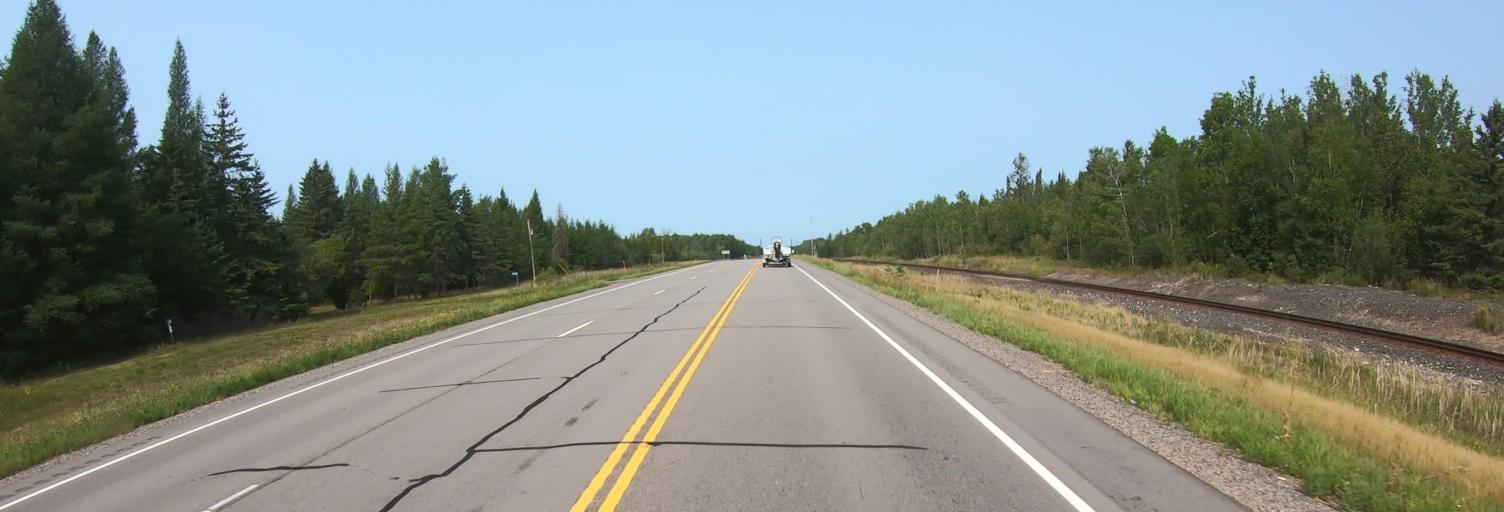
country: CA
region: Ontario
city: Fort Frances
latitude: 48.4457
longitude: -93.2632
